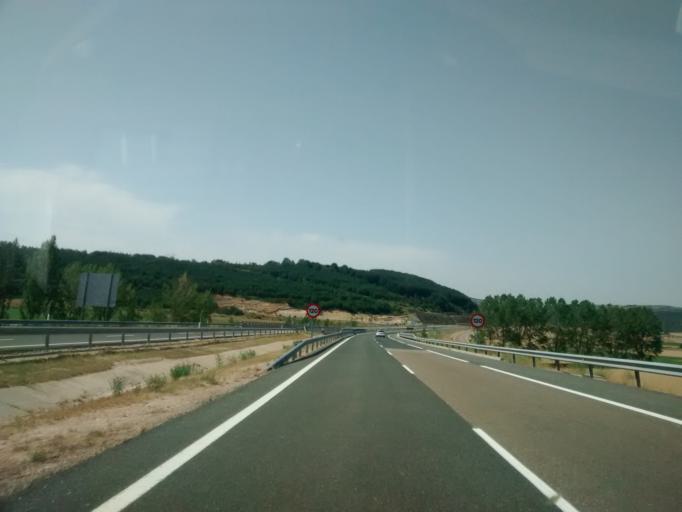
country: ES
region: Castille and Leon
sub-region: Provincia de Palencia
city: Aguilar de Campoo
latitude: 42.7659
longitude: -4.2812
